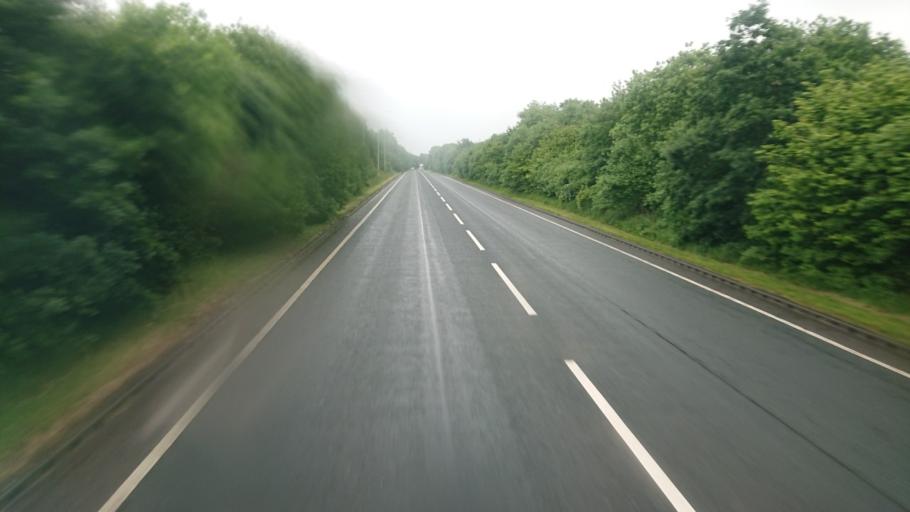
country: GB
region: England
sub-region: Lancashire
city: Morecambe
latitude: 54.0401
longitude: -2.8621
